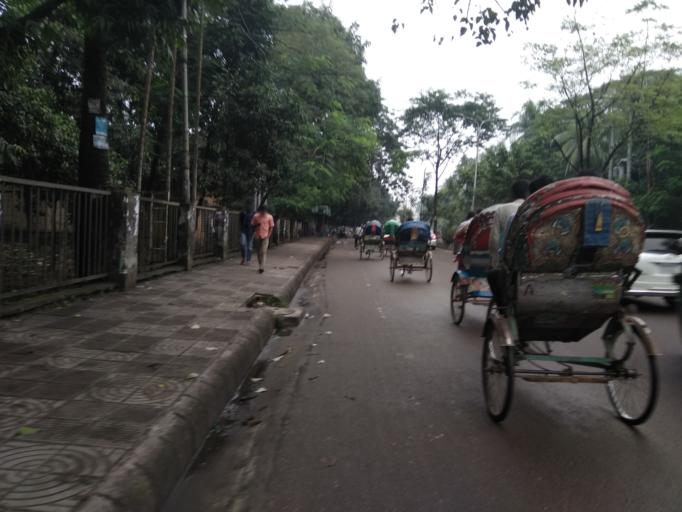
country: BD
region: Dhaka
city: Azimpur
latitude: 23.7337
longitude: 90.3955
